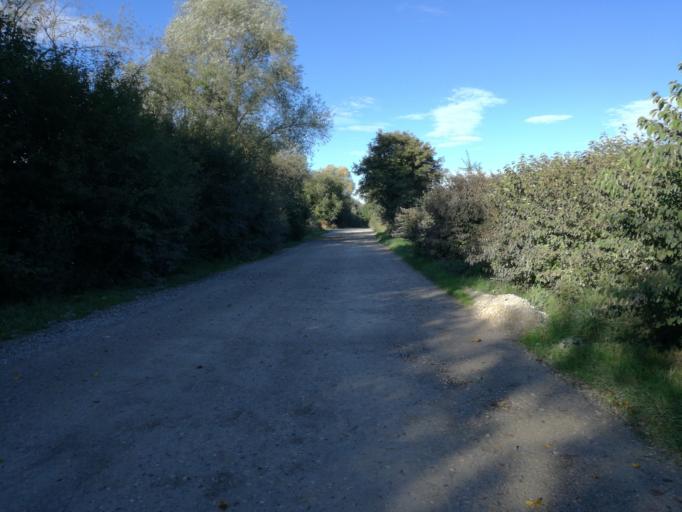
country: DE
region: Bavaria
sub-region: Upper Bavaria
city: Planegg
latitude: 48.0964
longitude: 11.4334
